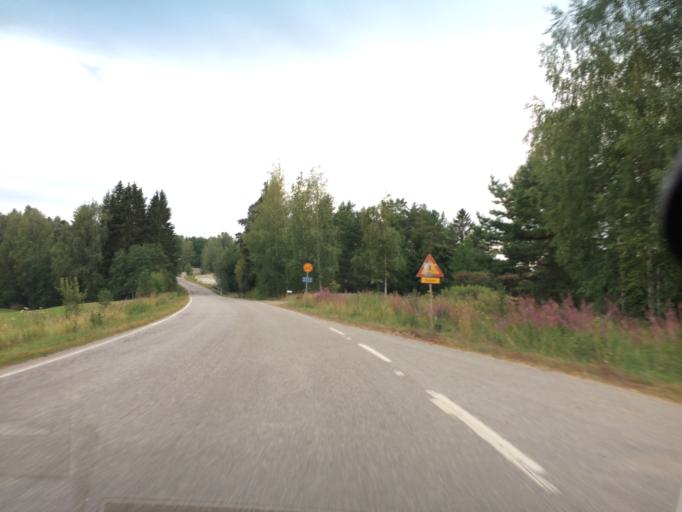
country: FI
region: Pirkanmaa
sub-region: Tampere
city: Luopioinen
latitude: 61.2570
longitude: 24.7086
